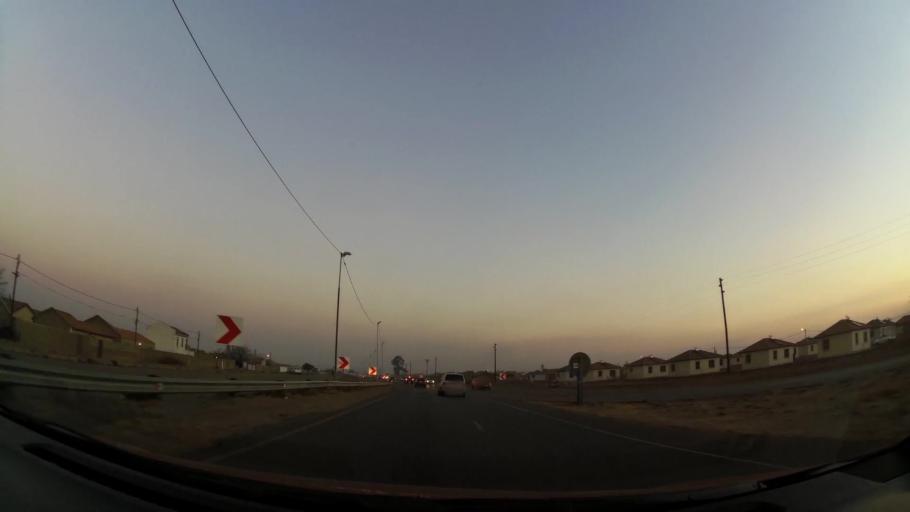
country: ZA
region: Gauteng
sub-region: City of Johannesburg Metropolitan Municipality
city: Soweto
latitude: -26.2318
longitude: 27.8037
